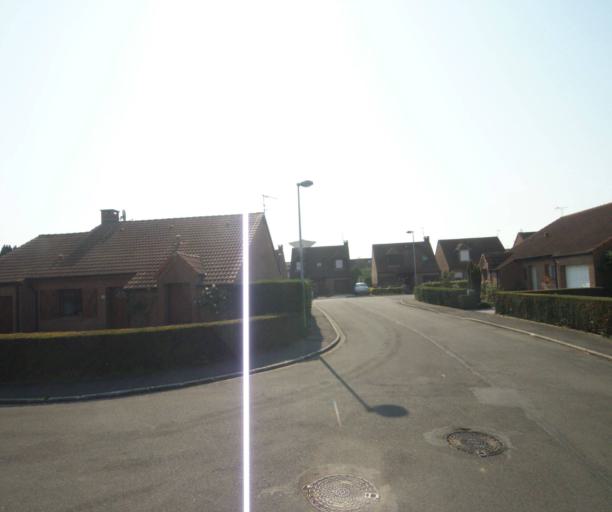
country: FR
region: Nord-Pas-de-Calais
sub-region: Departement du Nord
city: Quesnoy-sur-Deule
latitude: 50.7153
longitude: 2.9993
